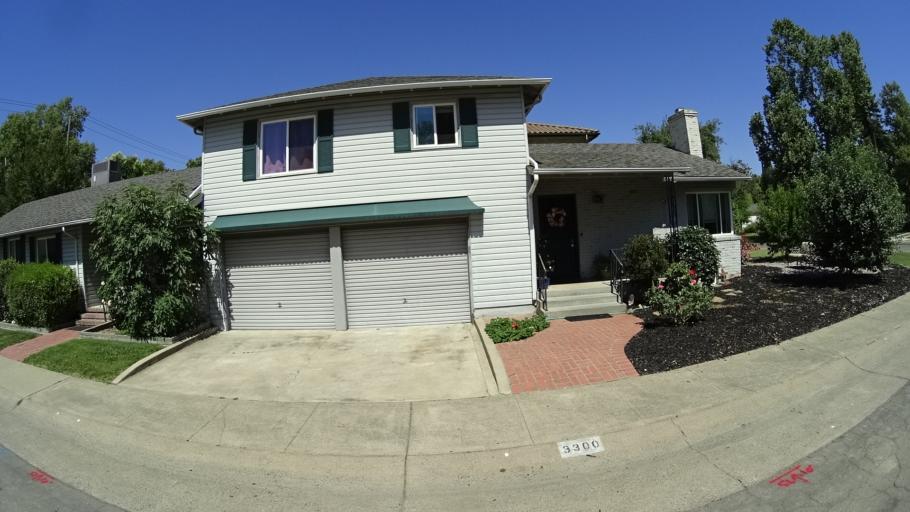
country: US
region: California
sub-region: Sacramento County
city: Sacramento
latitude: 38.5486
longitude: -121.5025
